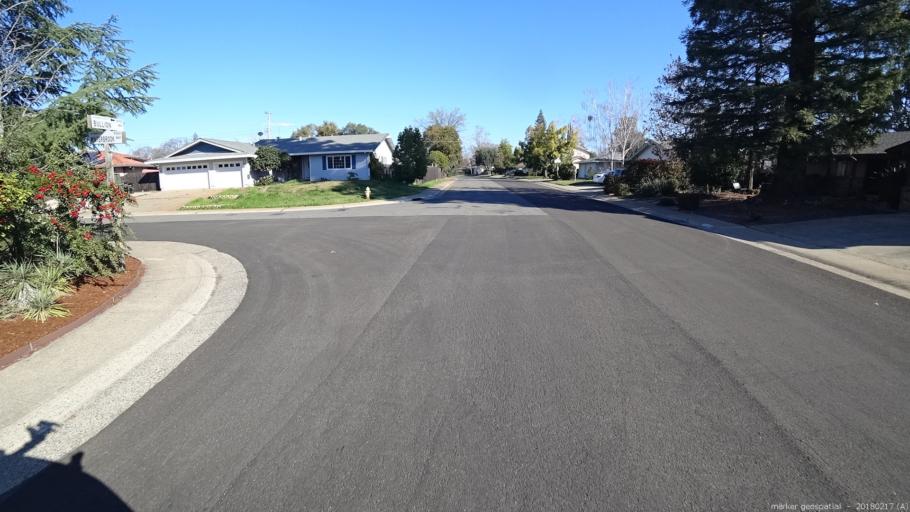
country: US
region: California
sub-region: Sacramento County
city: Folsom
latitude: 38.6612
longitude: -121.1972
